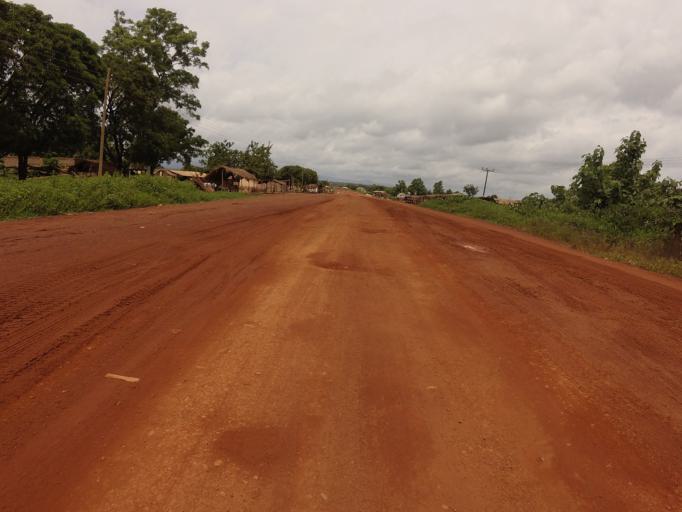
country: GH
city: Kpandae
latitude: 8.4041
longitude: 0.4002
